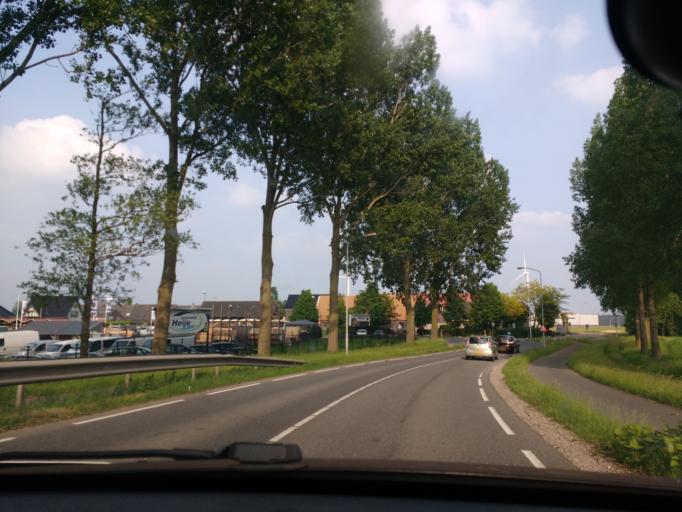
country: NL
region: Gelderland
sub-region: Gemeente Ede
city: Ederveen
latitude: 52.0337
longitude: 5.5960
